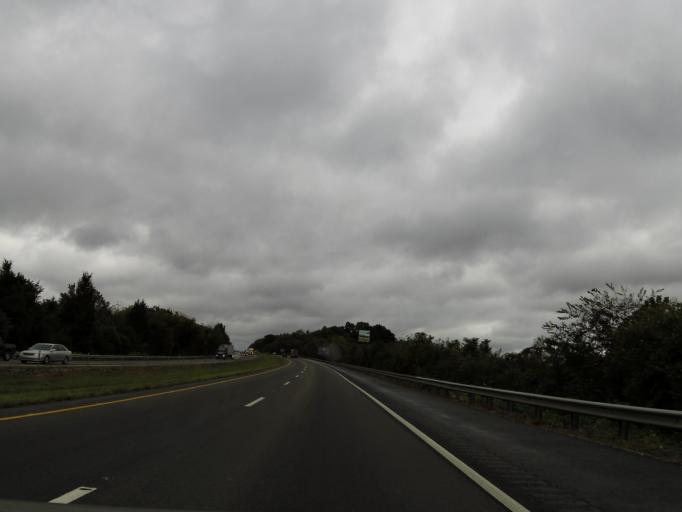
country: US
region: Tennessee
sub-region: Loudon County
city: Loudon
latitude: 35.7540
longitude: -84.3774
